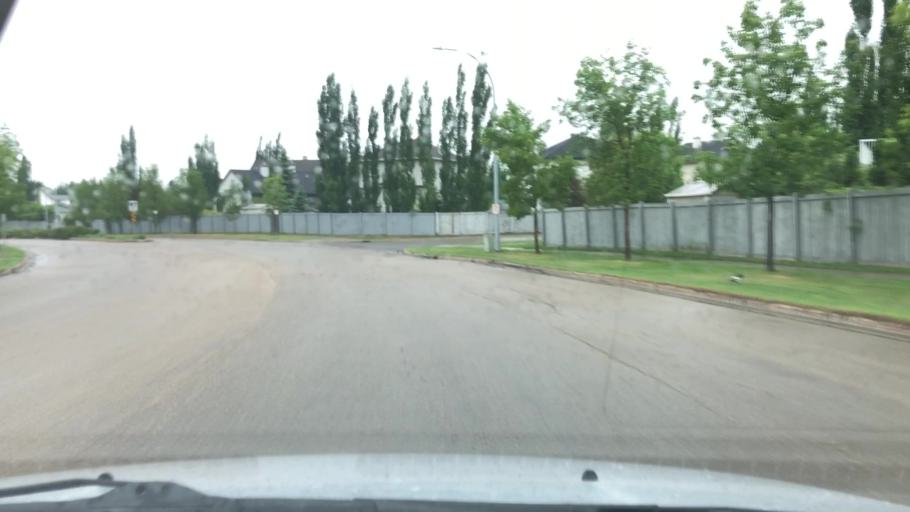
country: CA
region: Alberta
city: Sherwood Park
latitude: 53.5374
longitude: -113.2610
